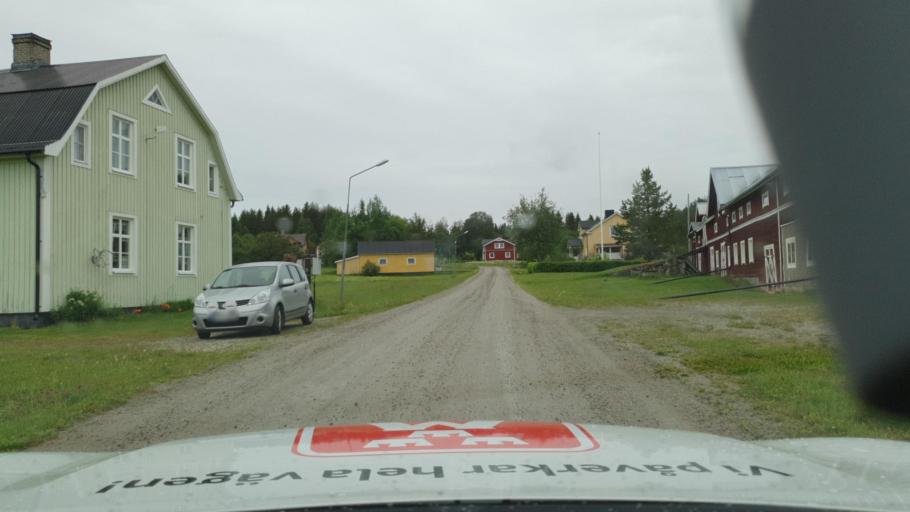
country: SE
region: Vaesterbotten
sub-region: Asele Kommun
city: Asele
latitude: 63.9656
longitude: 17.1052
